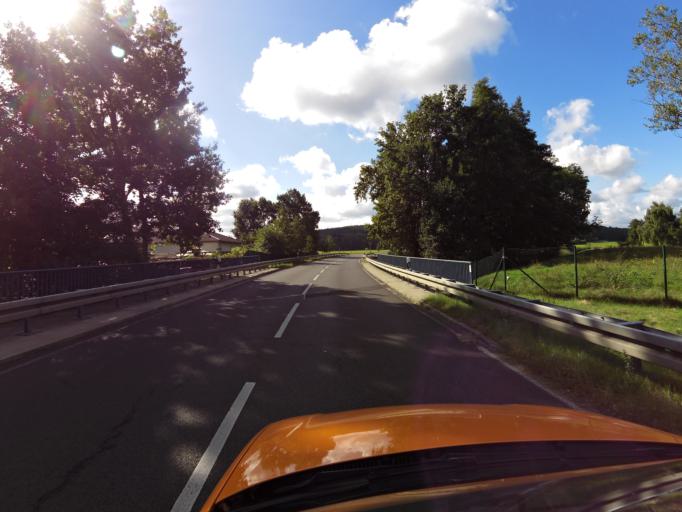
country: DE
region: Brandenburg
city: Michendorf
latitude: 52.3217
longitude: 13.1192
